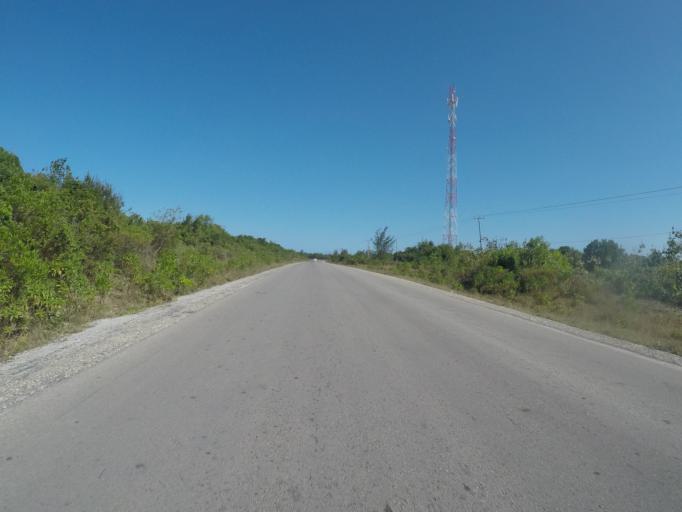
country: TZ
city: Kiwengwa
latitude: -6.1580
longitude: 39.5194
